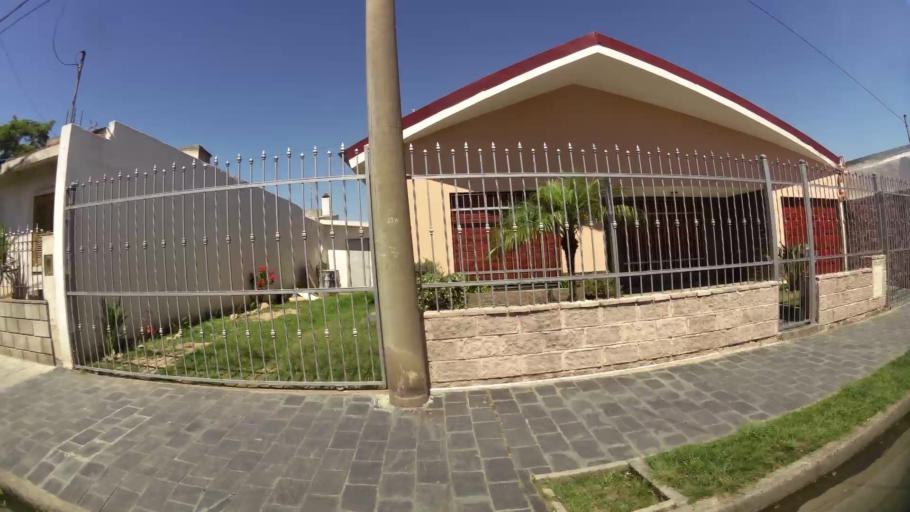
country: AR
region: Cordoba
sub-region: Departamento de Capital
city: Cordoba
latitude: -31.3794
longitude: -64.1582
